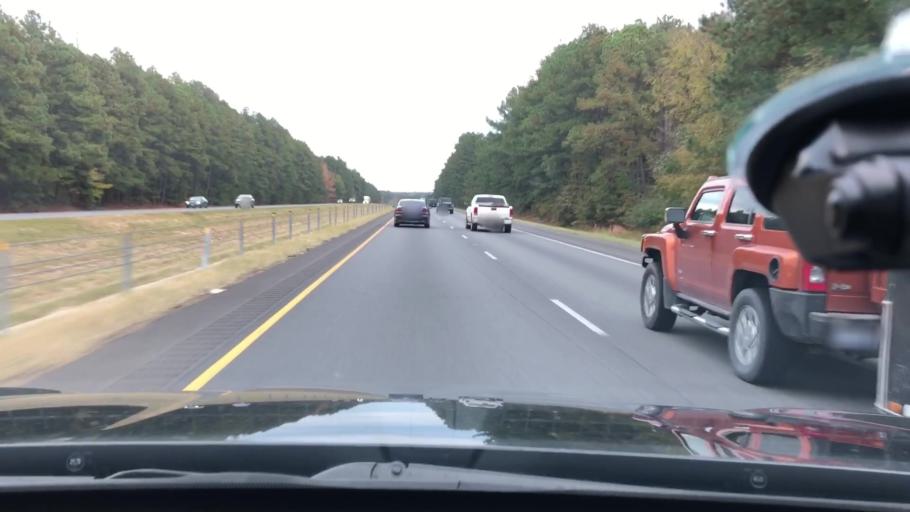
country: US
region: Arkansas
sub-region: Clark County
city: Arkadelphia
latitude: 34.2075
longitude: -93.0400
